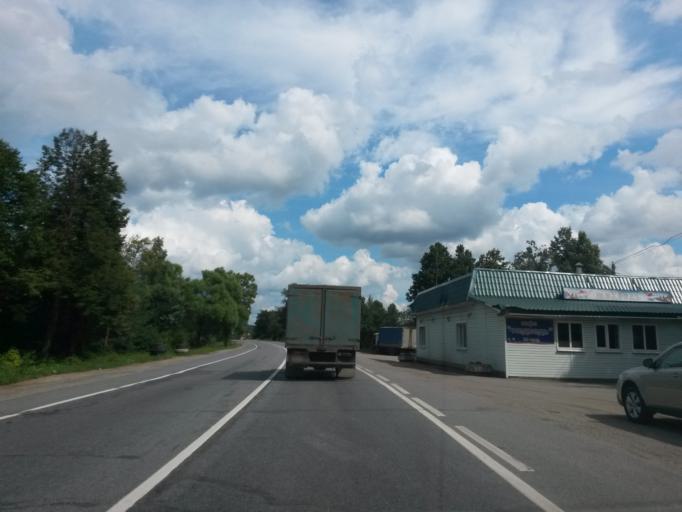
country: RU
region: Jaroslavl
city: Pereslavl'-Zalesskiy
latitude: 56.6517
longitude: 38.6982
